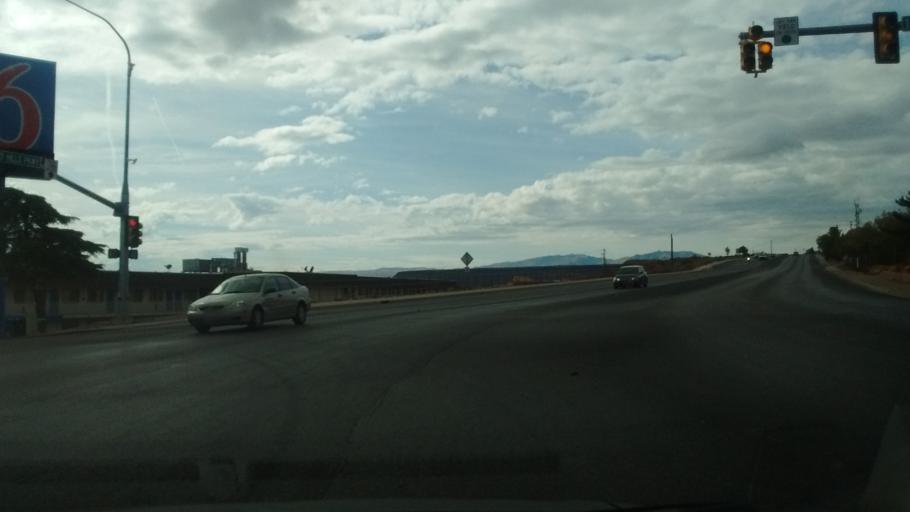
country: US
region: Utah
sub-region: Washington County
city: Saint George
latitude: 37.1122
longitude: -113.5621
